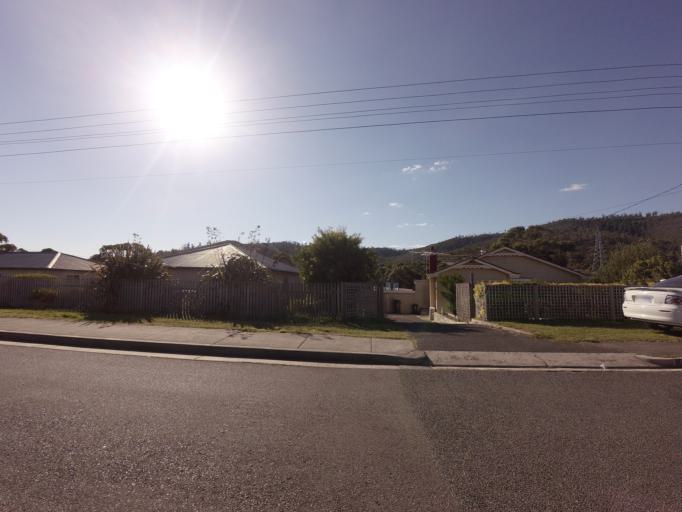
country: AU
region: Tasmania
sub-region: Clarence
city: Warrane
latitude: -42.8557
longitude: 147.3907
